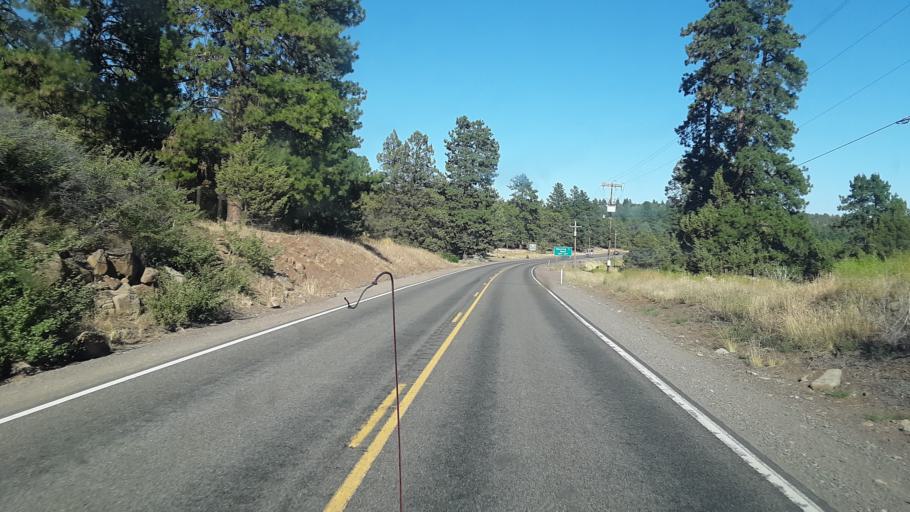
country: US
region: Oregon
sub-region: Klamath County
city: Klamath Falls
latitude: 42.2748
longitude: -121.8929
